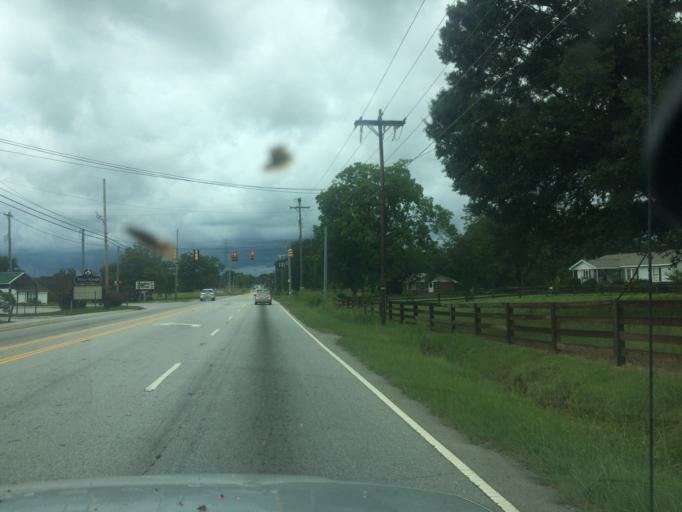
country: US
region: South Carolina
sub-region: Greenville County
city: Taylors
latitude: 34.9557
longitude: -82.2973
